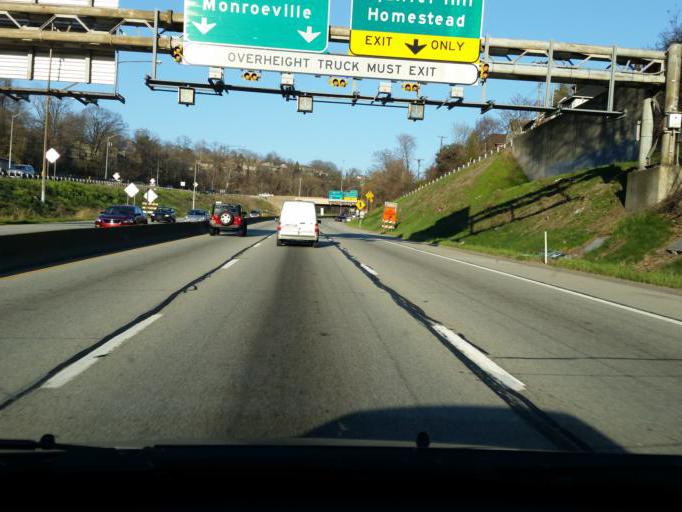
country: US
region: Pennsylvania
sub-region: Allegheny County
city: Homestead
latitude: 40.4286
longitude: -79.9350
